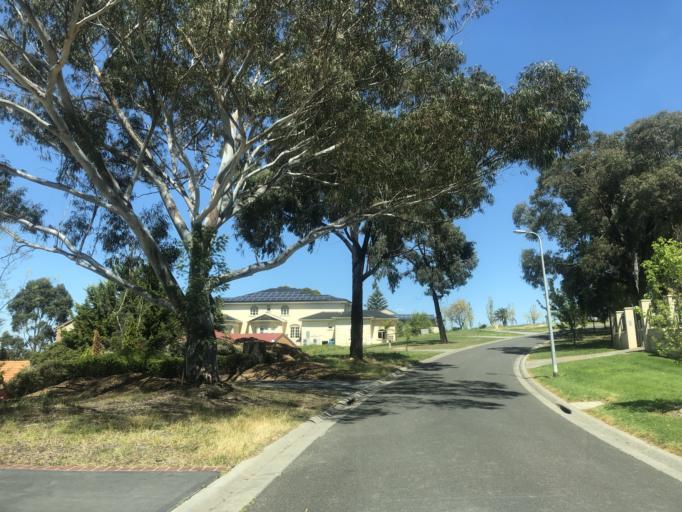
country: AU
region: Victoria
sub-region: Casey
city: Narre Warren North
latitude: -37.9826
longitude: 145.2881
